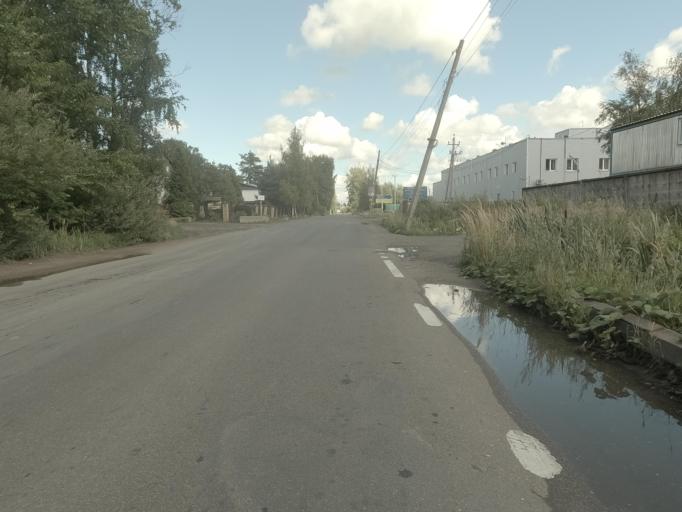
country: RU
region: Leningrad
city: Yanino Vtoroye
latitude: 59.9782
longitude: 30.5533
